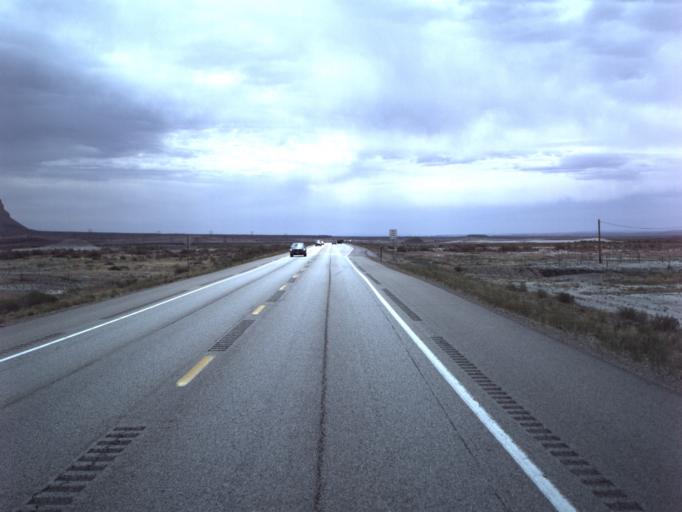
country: US
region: Utah
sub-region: Carbon County
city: East Carbon City
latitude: 39.1283
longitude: -110.3355
